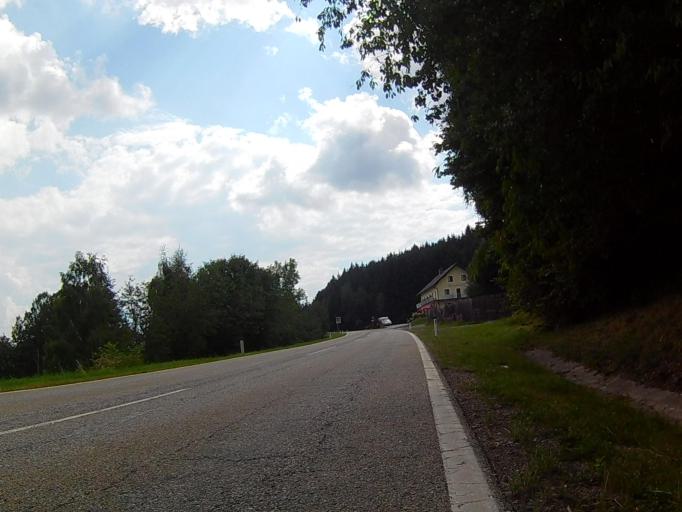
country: AT
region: Styria
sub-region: Politischer Bezirk Deutschlandsberg
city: Soboth
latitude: 46.6866
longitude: 15.1004
